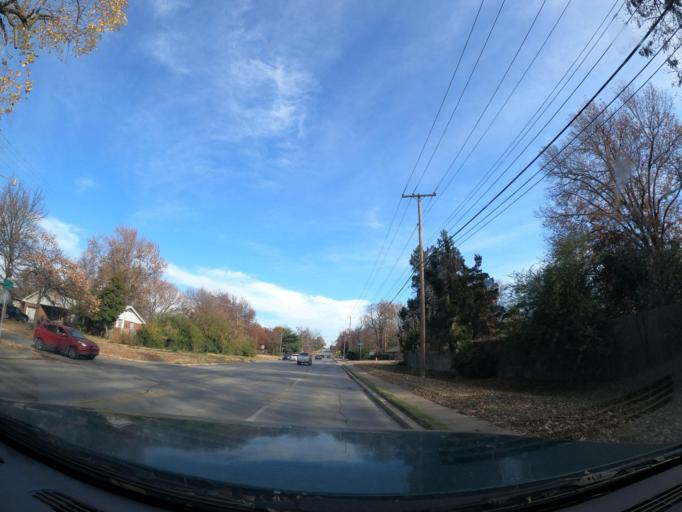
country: US
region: Oklahoma
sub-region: Tulsa County
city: Tulsa
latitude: 36.1043
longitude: -95.9325
